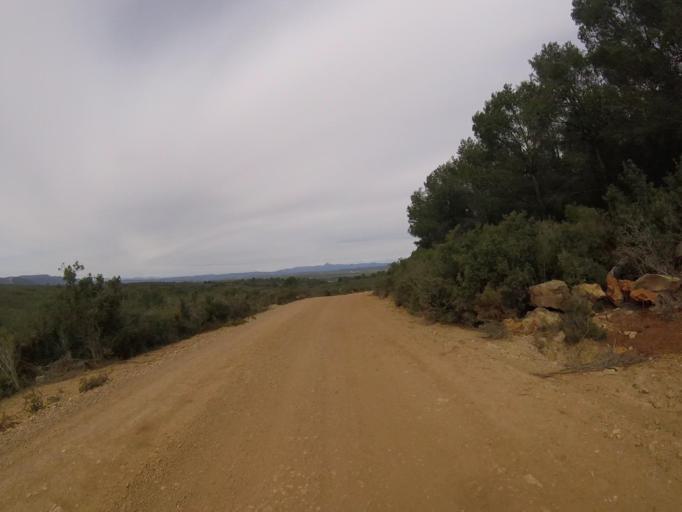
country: ES
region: Valencia
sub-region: Provincia de Castello
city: Benlloch
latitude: 40.1955
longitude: 0.0725
